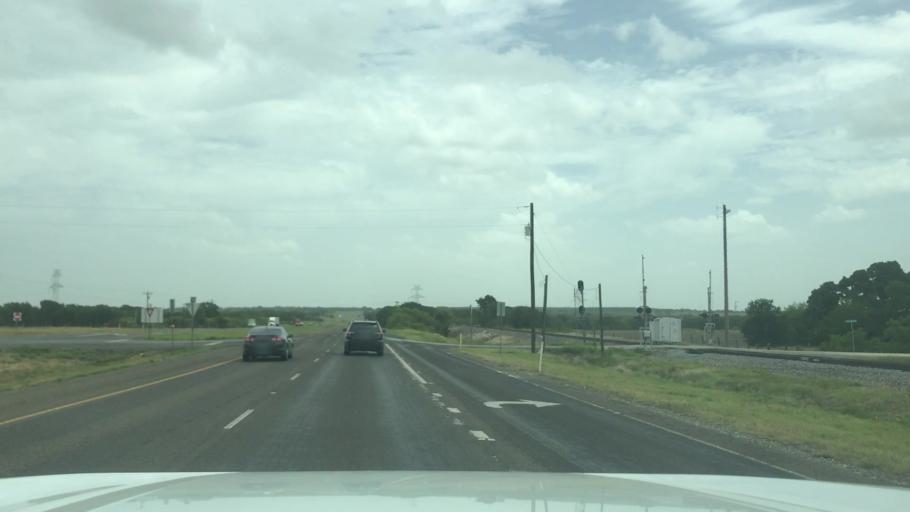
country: US
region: Texas
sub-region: McLennan County
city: Riesel
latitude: 31.5105
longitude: -96.9521
